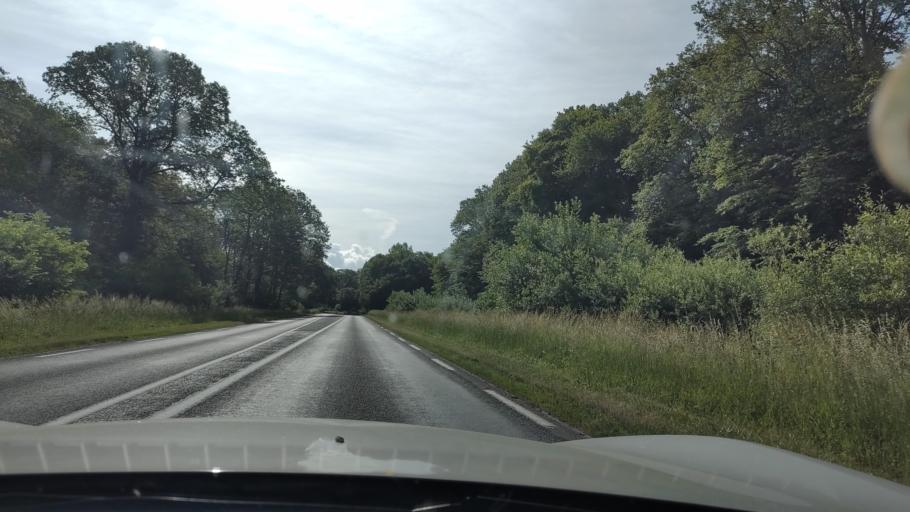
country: FR
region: Ile-de-France
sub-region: Departement de Seine-et-Marne
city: Sourdun
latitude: 48.5290
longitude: 3.4006
